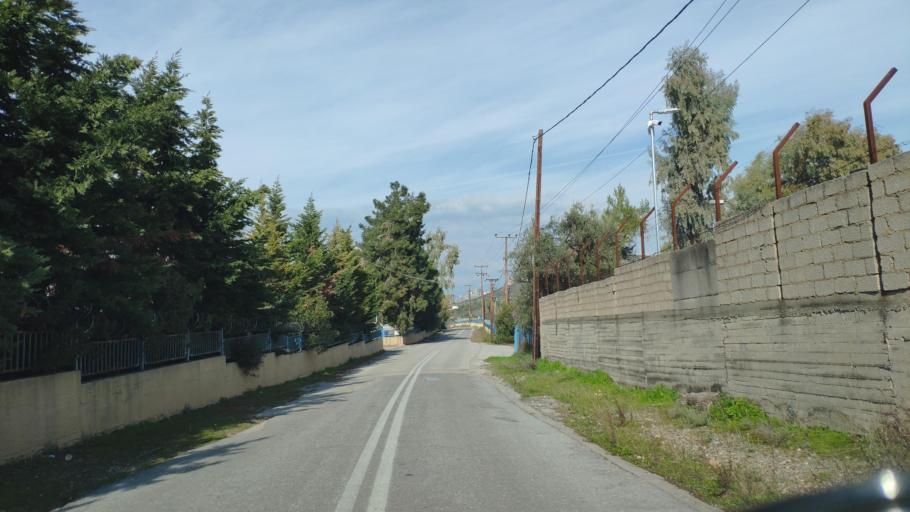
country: GR
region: Central Greece
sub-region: Nomos Evvoias
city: Vathi
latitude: 38.4176
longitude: 23.5912
